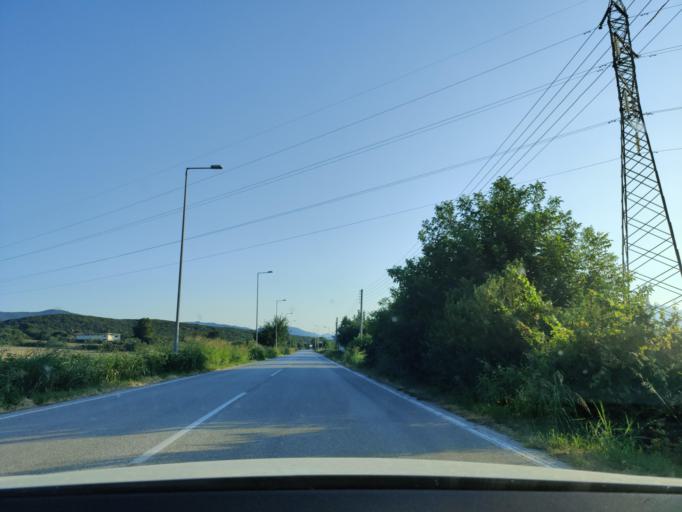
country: GR
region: East Macedonia and Thrace
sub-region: Nomos Kavalas
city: Amygdaleonas
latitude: 40.9807
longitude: 24.3673
